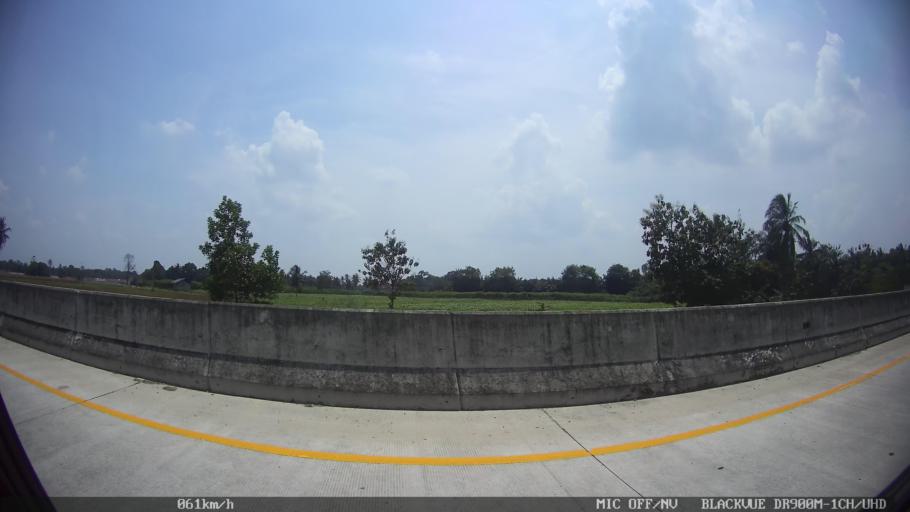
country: ID
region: Lampung
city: Natar
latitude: -5.3100
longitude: 105.2524
